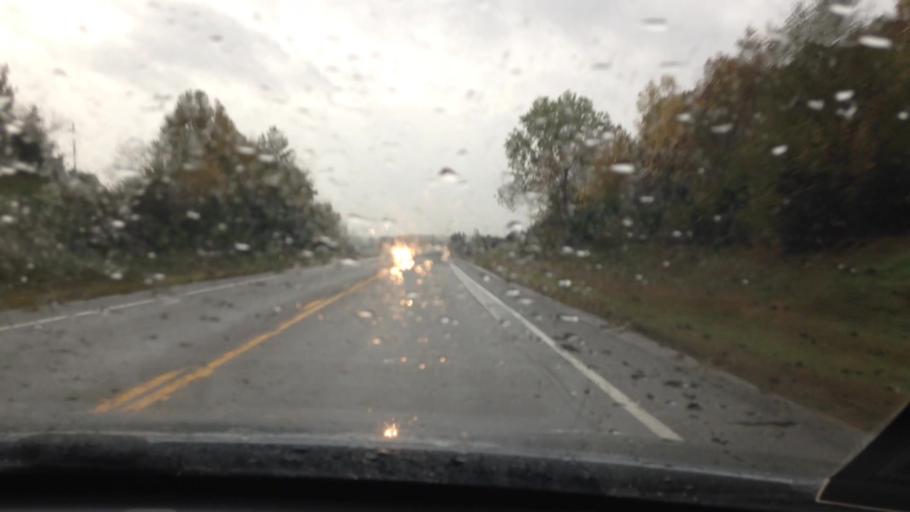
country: US
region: Missouri
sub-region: Platte County
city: Weston
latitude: 39.3927
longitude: -94.8483
